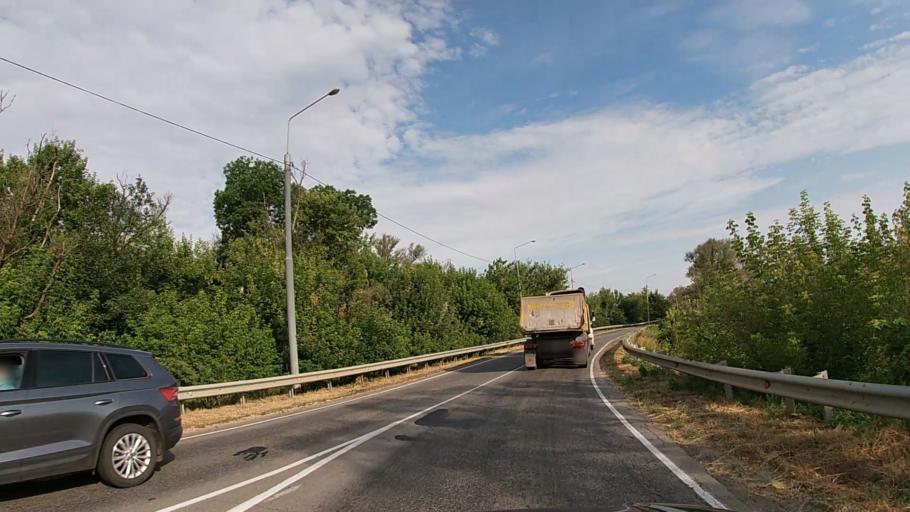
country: RU
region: Belgorod
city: Severnyy
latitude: 50.6339
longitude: 36.4647
